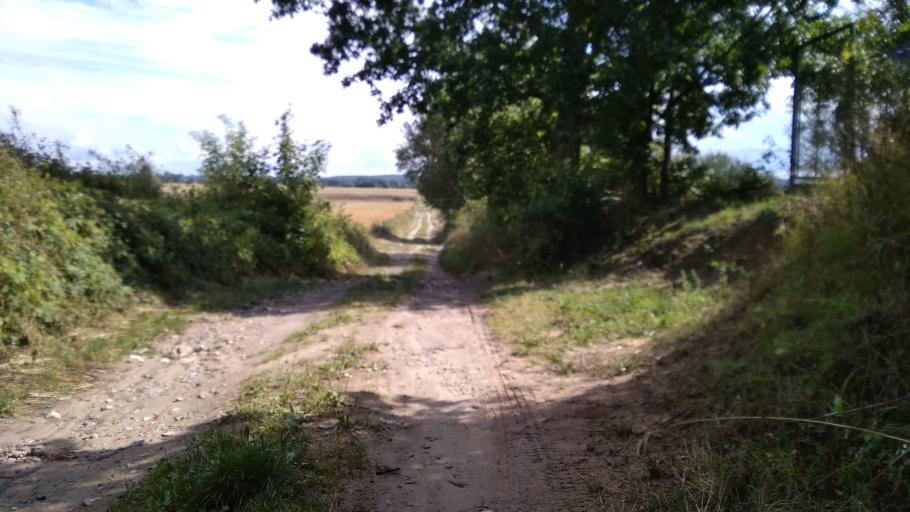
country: PL
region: West Pomeranian Voivodeship
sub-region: Powiat slawienski
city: Darlowo
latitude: 54.5096
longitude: 16.5164
